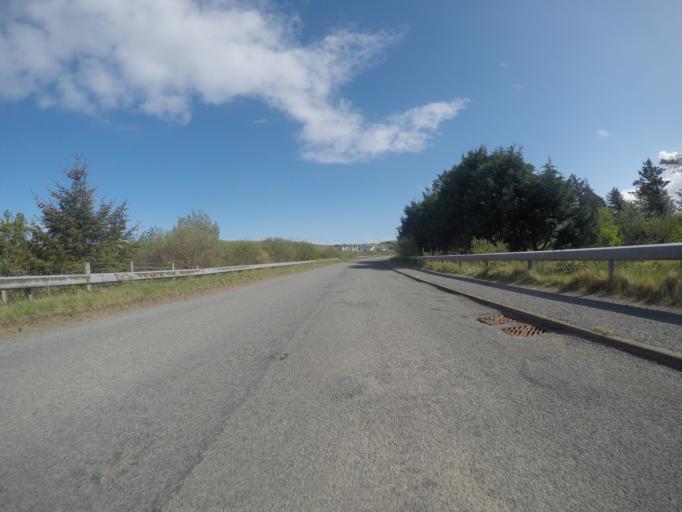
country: GB
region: Scotland
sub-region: Highland
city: Portree
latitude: 57.6300
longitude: -6.2118
